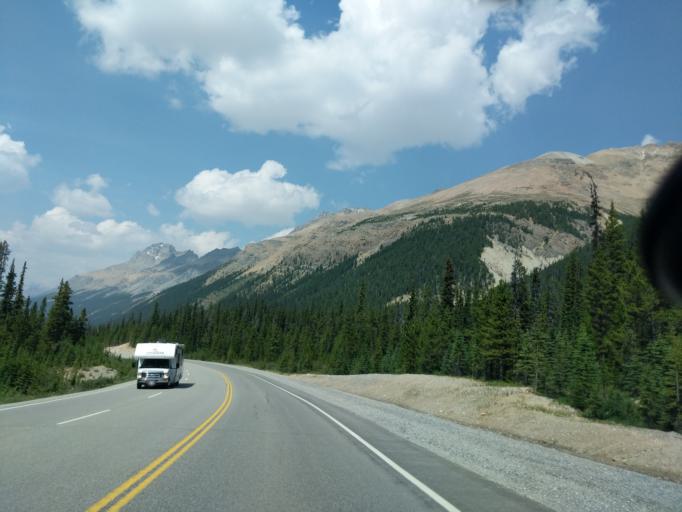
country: CA
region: Alberta
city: Lake Louise
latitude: 51.7286
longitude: -116.5009
